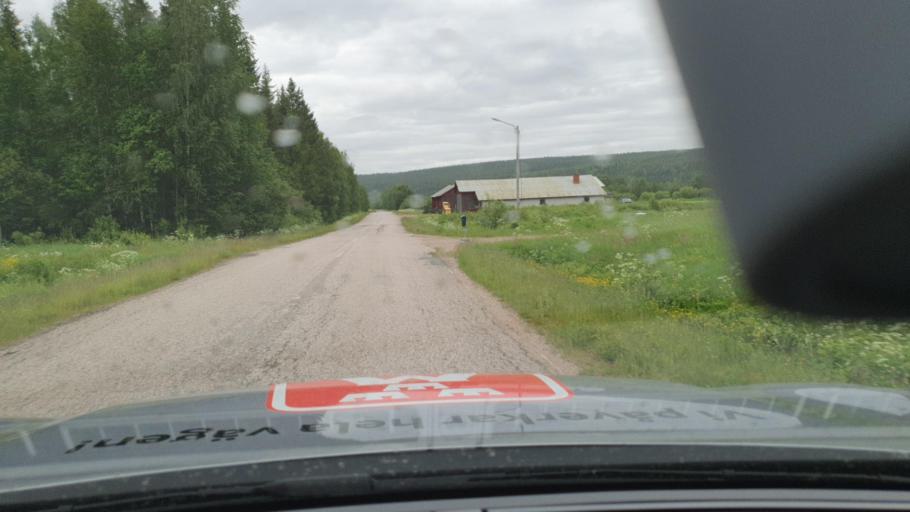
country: SE
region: Norrbotten
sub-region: Overkalix Kommun
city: OEverkalix
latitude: 66.4684
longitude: 22.7693
